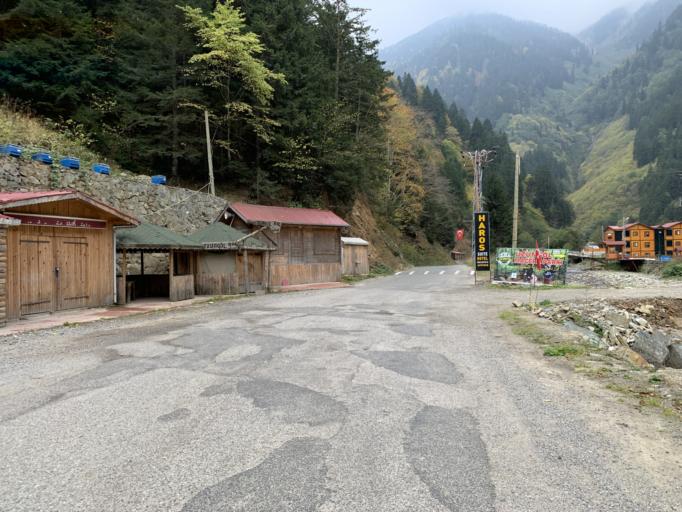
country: TR
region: Trabzon
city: Uzungol
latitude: 40.5980
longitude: 40.3214
